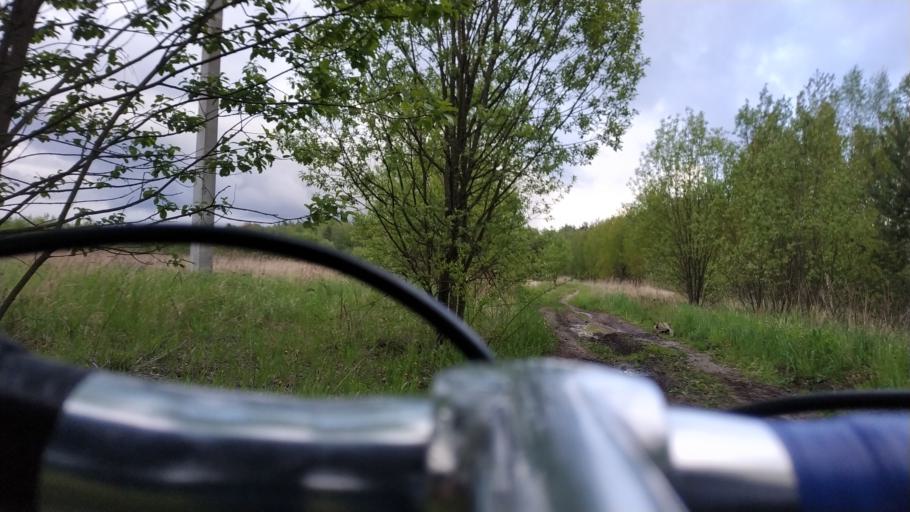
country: RU
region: Moskovskaya
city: Ramenskoye
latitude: 55.5995
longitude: 38.2833
